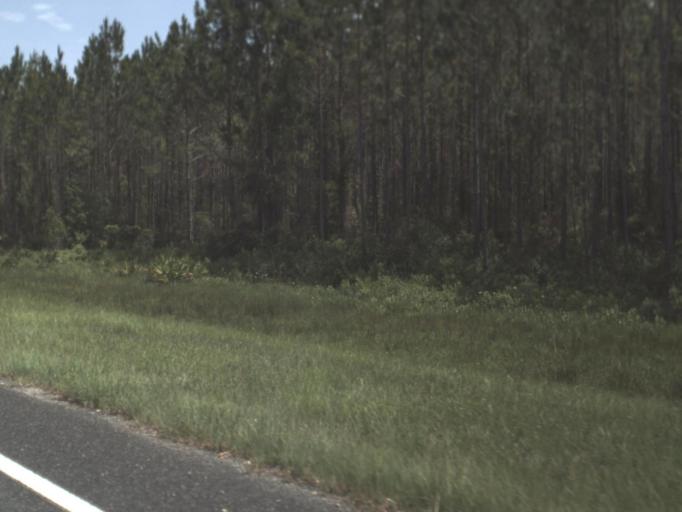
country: US
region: Florida
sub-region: Taylor County
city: Steinhatchee
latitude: 29.7234
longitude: -83.3088
